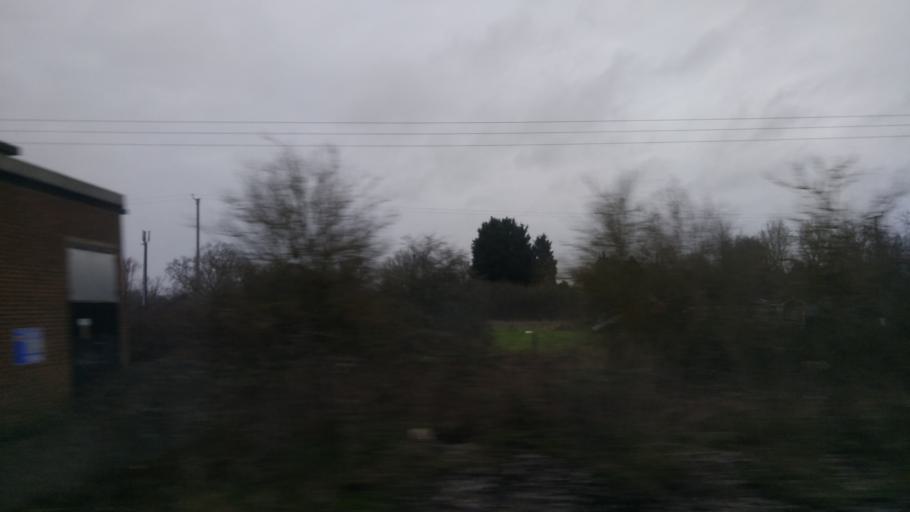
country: GB
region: England
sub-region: Kent
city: Staplehurst
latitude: 51.1709
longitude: 0.5590
